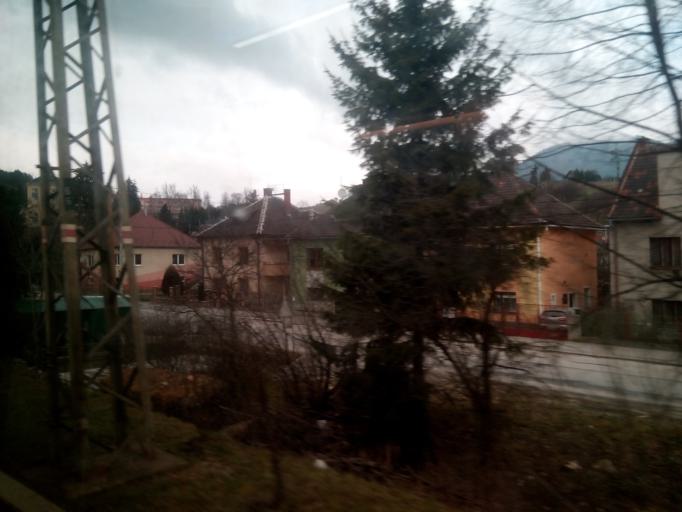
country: SK
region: Zilinsky
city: Ruzomberok
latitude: 49.0861
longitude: 19.3053
